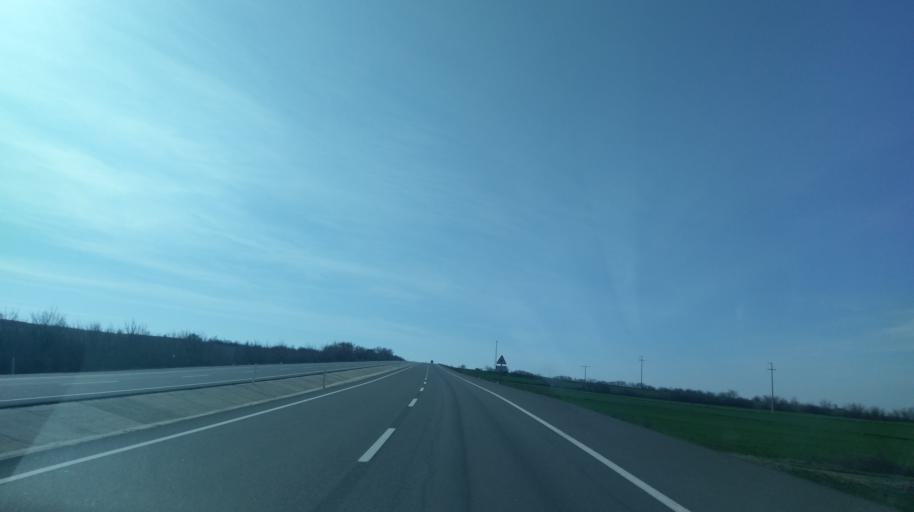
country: TR
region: Edirne
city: Hamidiye
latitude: 41.0867
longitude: 26.6401
